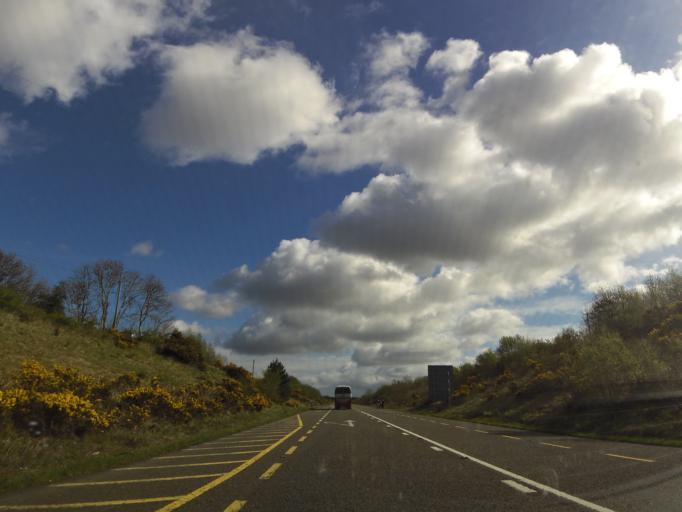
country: IE
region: Connaught
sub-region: Maigh Eo
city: Kiltamagh
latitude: 53.8022
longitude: -8.9161
